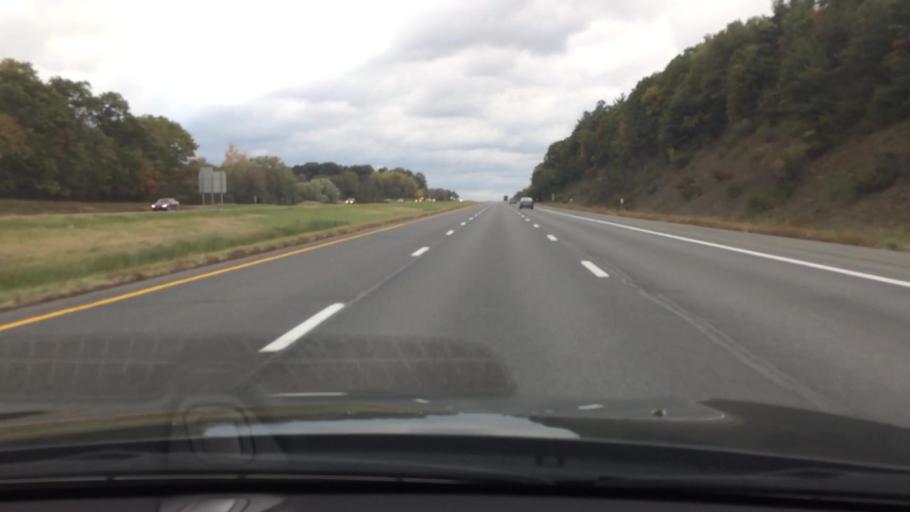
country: US
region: New York
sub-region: Rensselaer County
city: East Greenbush
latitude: 42.6133
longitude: -73.6883
